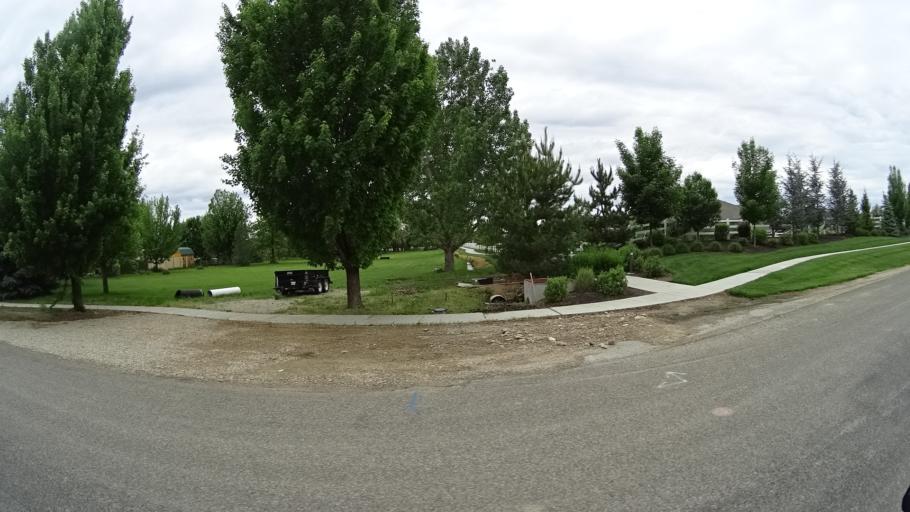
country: US
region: Idaho
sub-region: Ada County
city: Eagle
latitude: 43.7114
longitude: -116.3935
